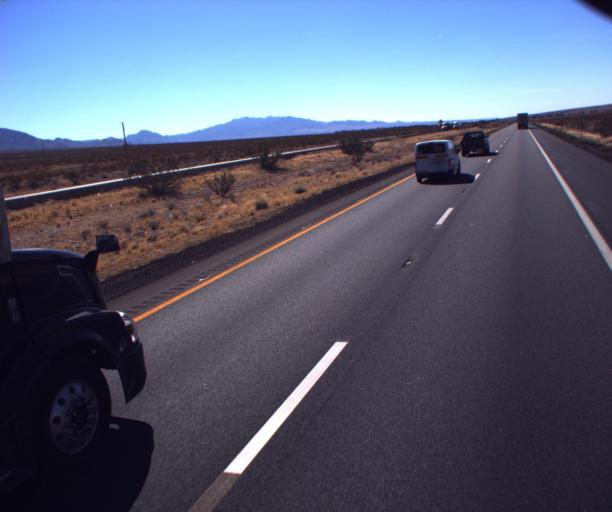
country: US
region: Arizona
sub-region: Mohave County
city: Beaver Dam
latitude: 36.9135
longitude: -113.8809
